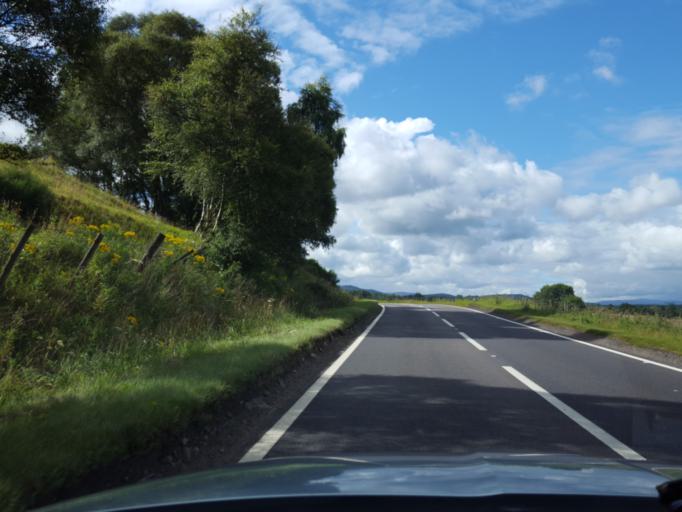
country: GB
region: Scotland
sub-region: Highland
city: Grantown on Spey
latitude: 57.3496
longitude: -3.5249
